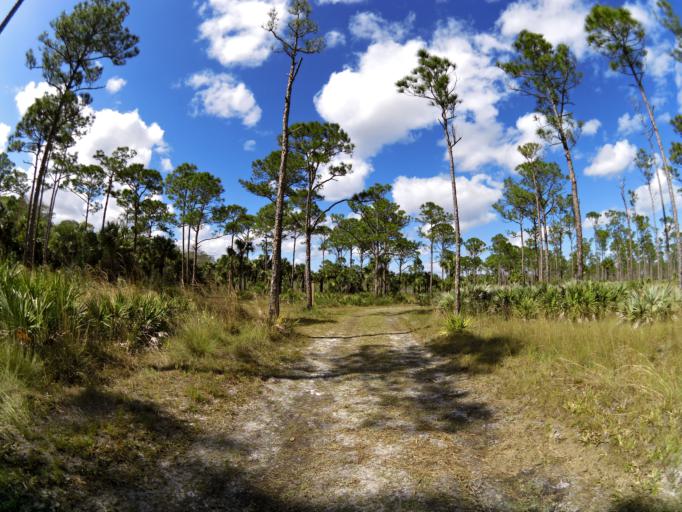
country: US
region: Florida
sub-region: Palm Beach County
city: Tequesta
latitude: 27.0107
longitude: -80.1626
